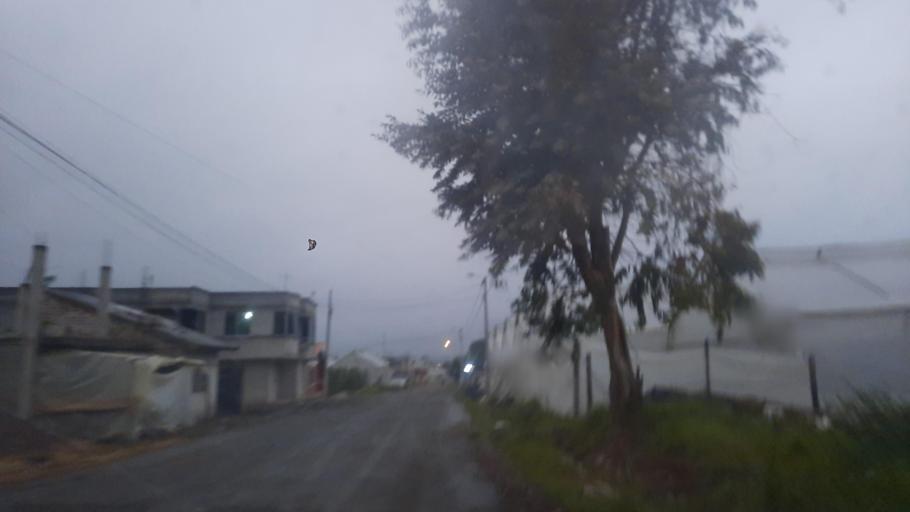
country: EC
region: Chimborazo
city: Riobamba
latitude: -1.6884
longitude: -78.6688
